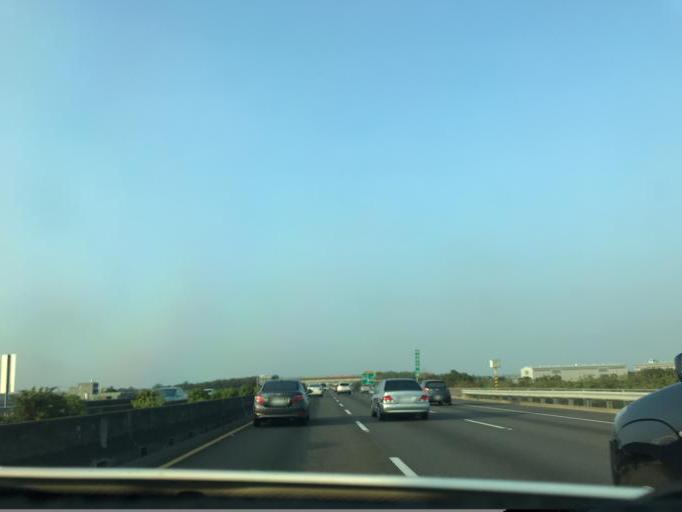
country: TW
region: Taiwan
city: Xinying
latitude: 23.2012
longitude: 120.2366
